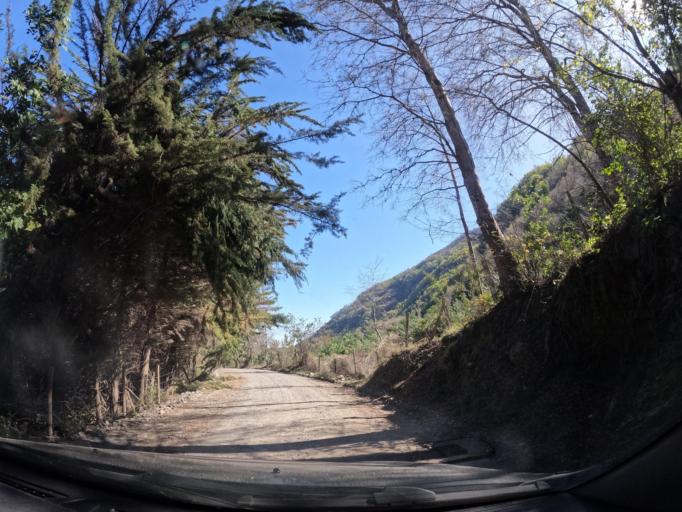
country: CL
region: Maule
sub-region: Provincia de Linares
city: Longavi
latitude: -36.2273
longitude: -71.3909
